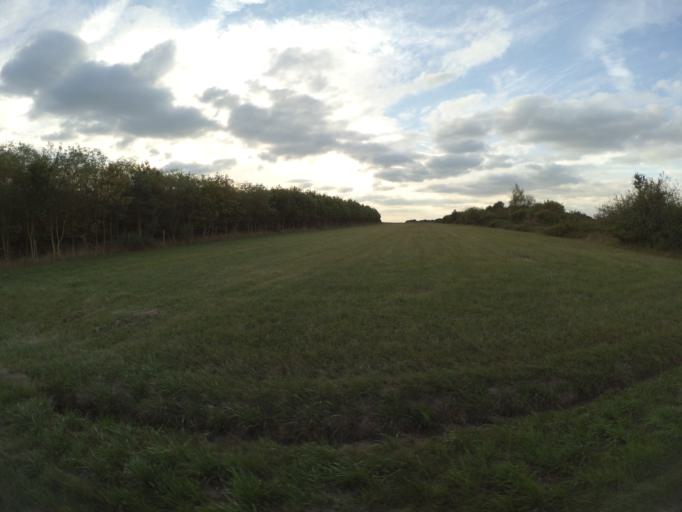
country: FR
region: Centre
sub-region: Departement d'Indre-et-Loire
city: Poce-sur-Cisse
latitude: 47.4540
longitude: 0.9702
